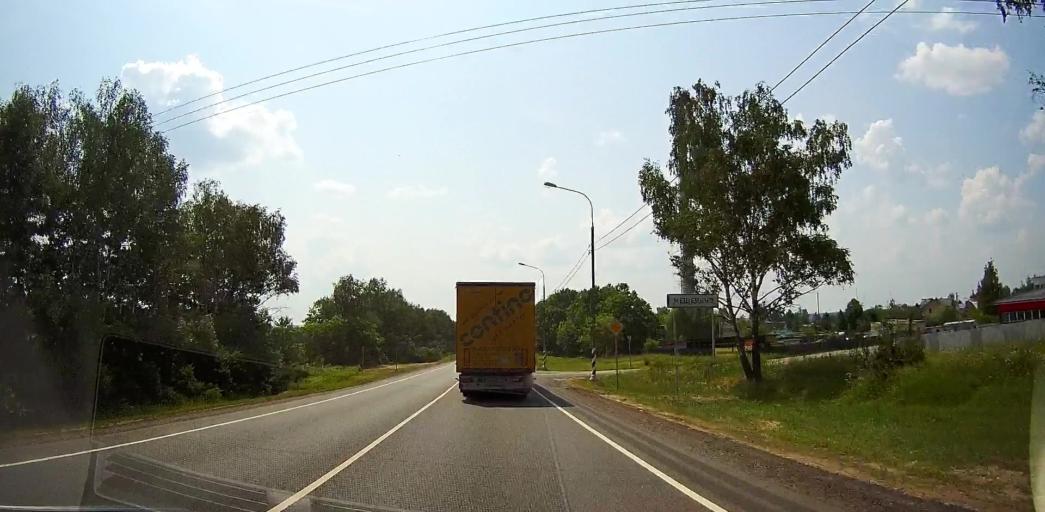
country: RU
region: Moskovskaya
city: Meshcherino
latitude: 55.1967
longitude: 38.3687
